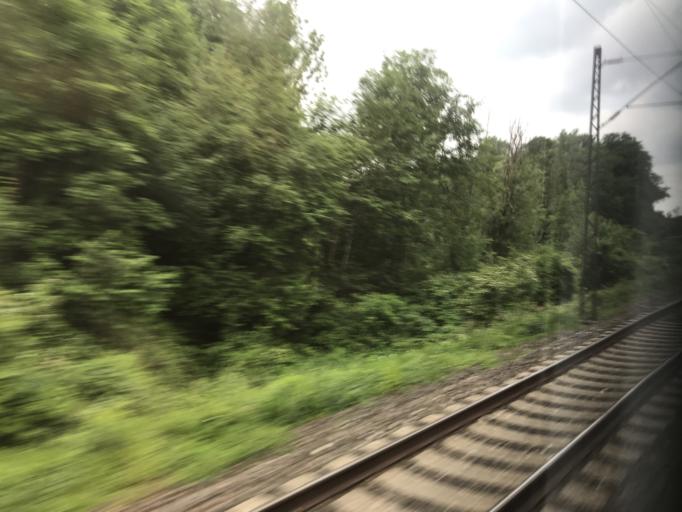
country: DE
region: Bavaria
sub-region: Swabia
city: Leipheim
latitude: 48.4600
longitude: 10.2433
